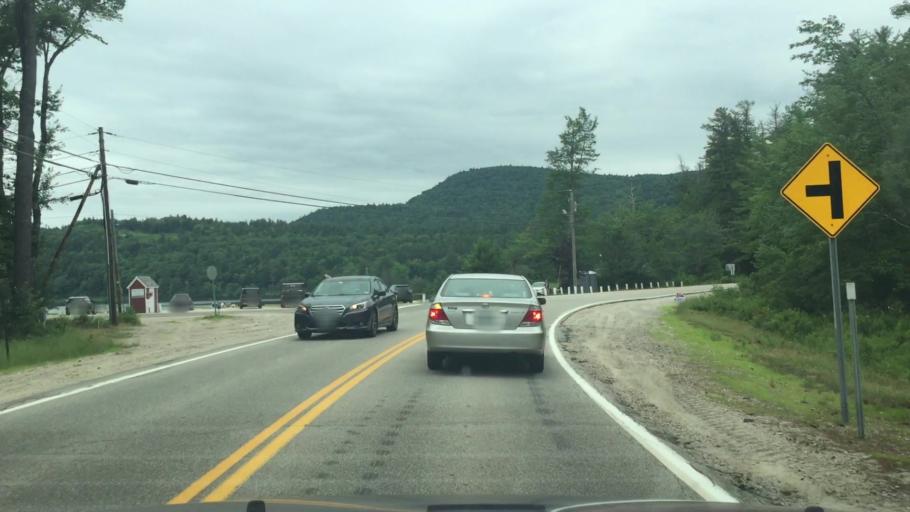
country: US
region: New Hampshire
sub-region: Carroll County
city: Madison
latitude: 43.9151
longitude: -71.0737
